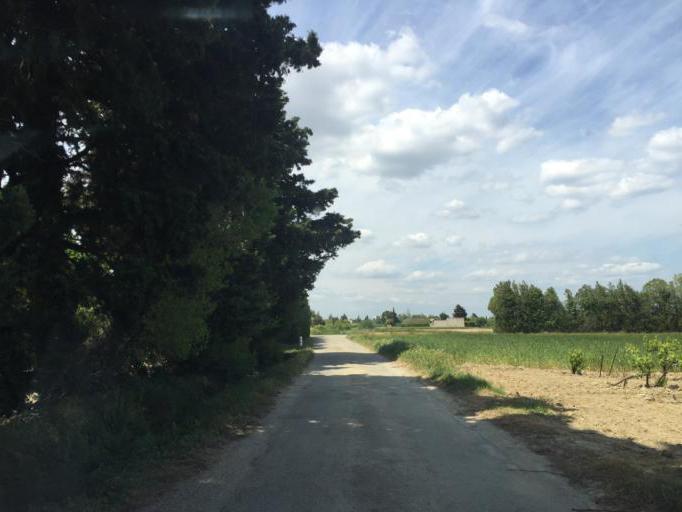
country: FR
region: Provence-Alpes-Cote d'Azur
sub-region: Departement du Vaucluse
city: Jonquieres
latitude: 44.1182
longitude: 4.9231
